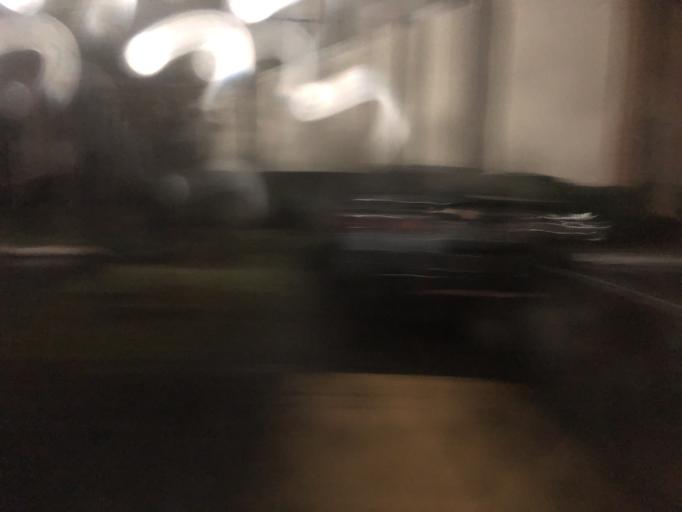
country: US
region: Florida
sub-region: Orange County
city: Azalea Park
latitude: 28.5130
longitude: -81.2997
